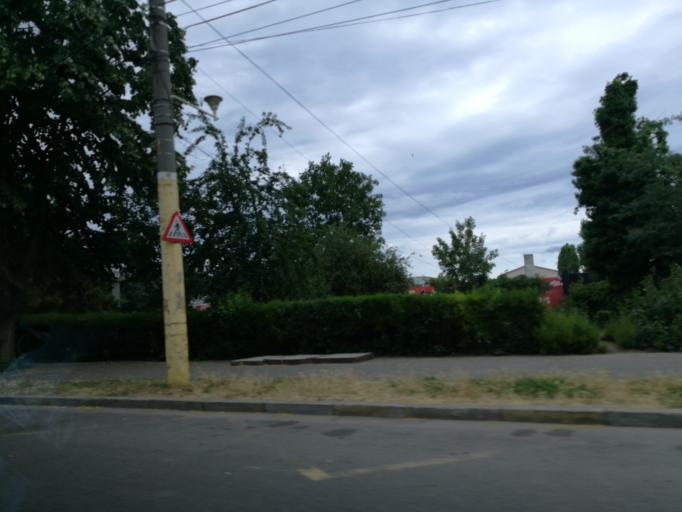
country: RO
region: Constanta
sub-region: Municipiul Constanta
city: Palazu Mare
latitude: 44.2138
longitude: 28.6285
